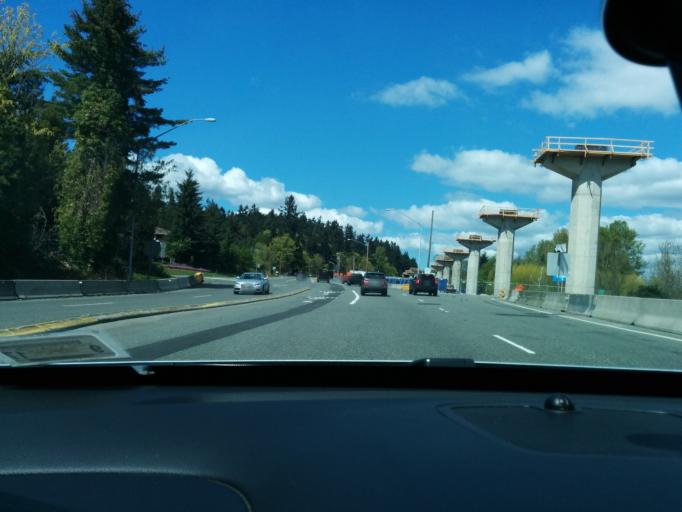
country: US
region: Washington
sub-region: King County
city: Newport
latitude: 47.5831
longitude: -122.1882
